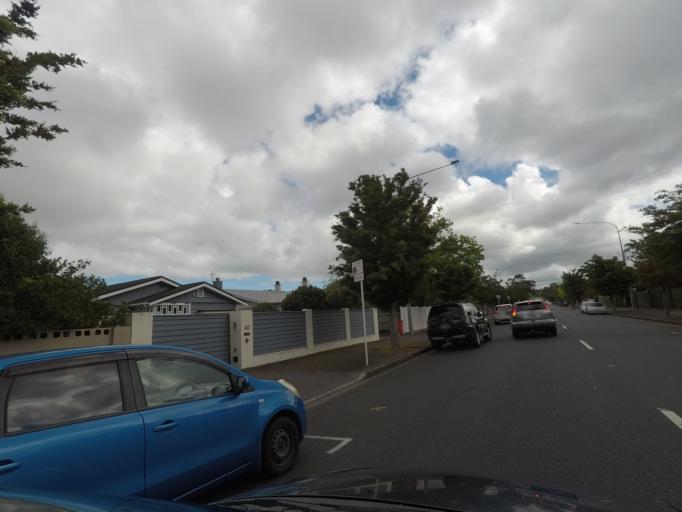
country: NZ
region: Auckland
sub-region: Auckland
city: Auckland
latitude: -36.8843
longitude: 174.8049
